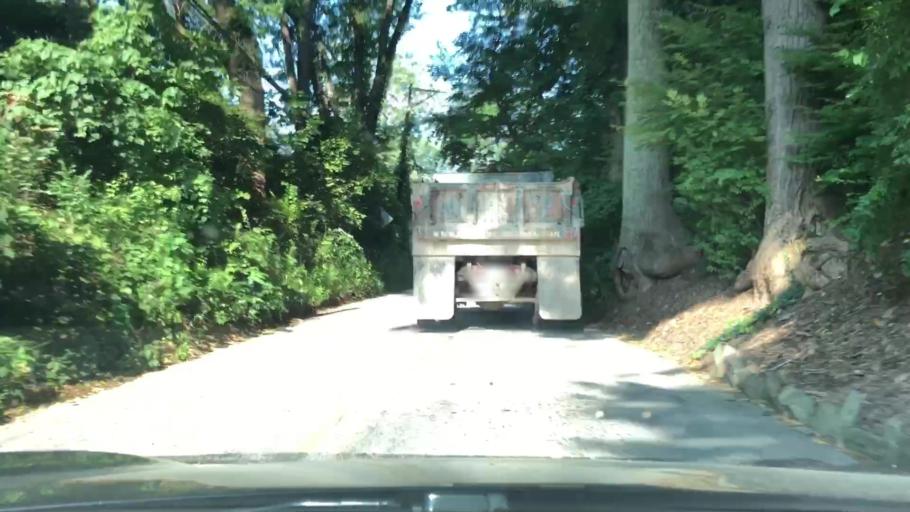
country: US
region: Pennsylvania
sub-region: Delaware County
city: Broomall
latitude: 40.0050
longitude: -75.3653
